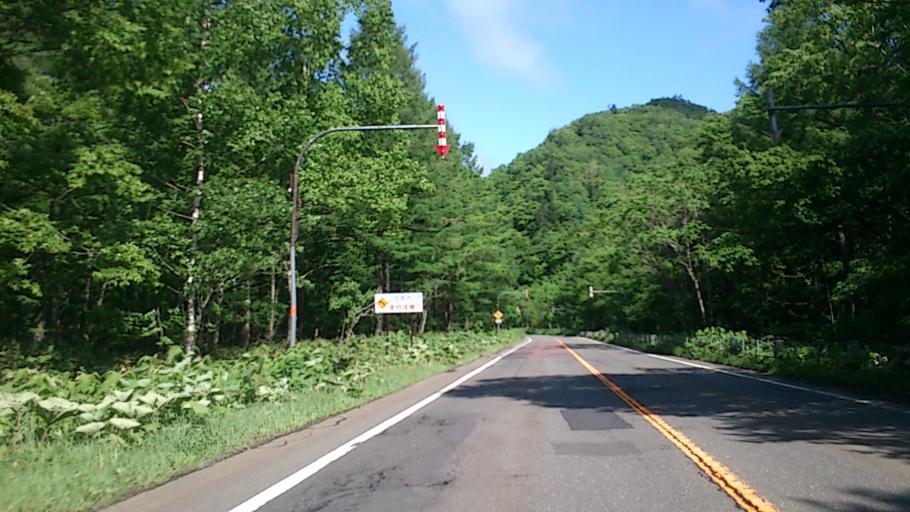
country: JP
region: Hokkaido
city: Shiraoi
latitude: 42.7158
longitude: 141.2260
